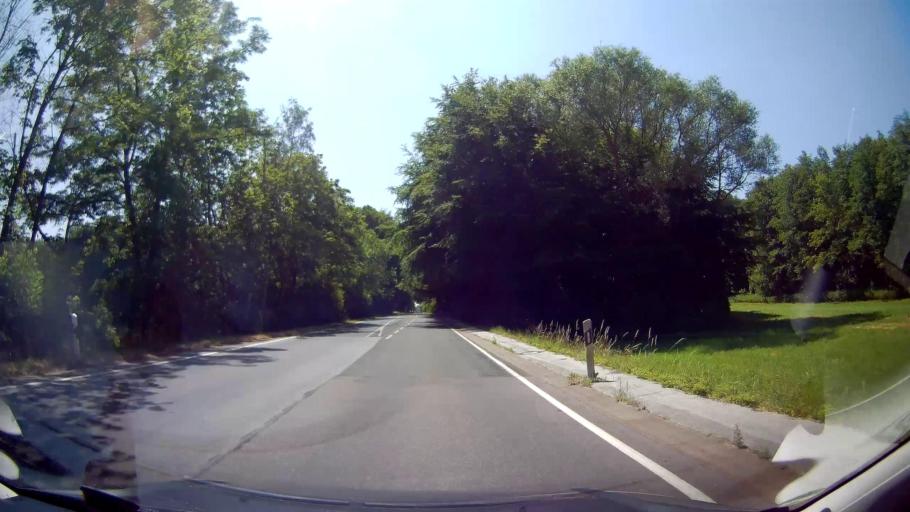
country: DE
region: North Rhine-Westphalia
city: Marl
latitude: 51.6388
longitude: 7.0461
